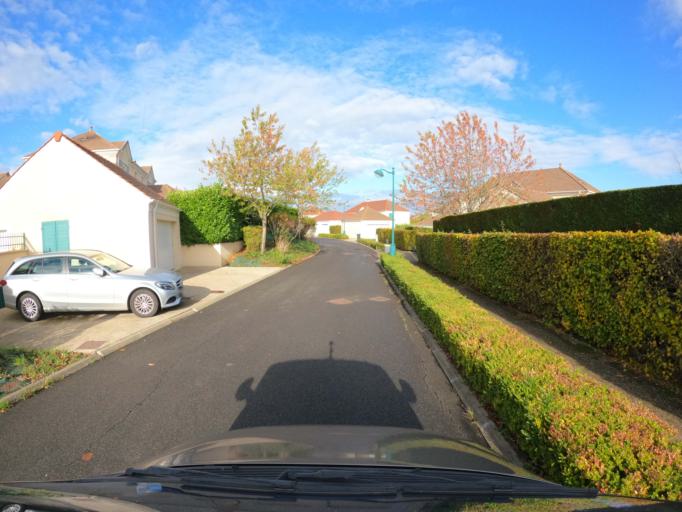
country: FR
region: Ile-de-France
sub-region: Departement de Seine-et-Marne
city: Magny-le-Hongre
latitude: 48.8679
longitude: 2.8233
